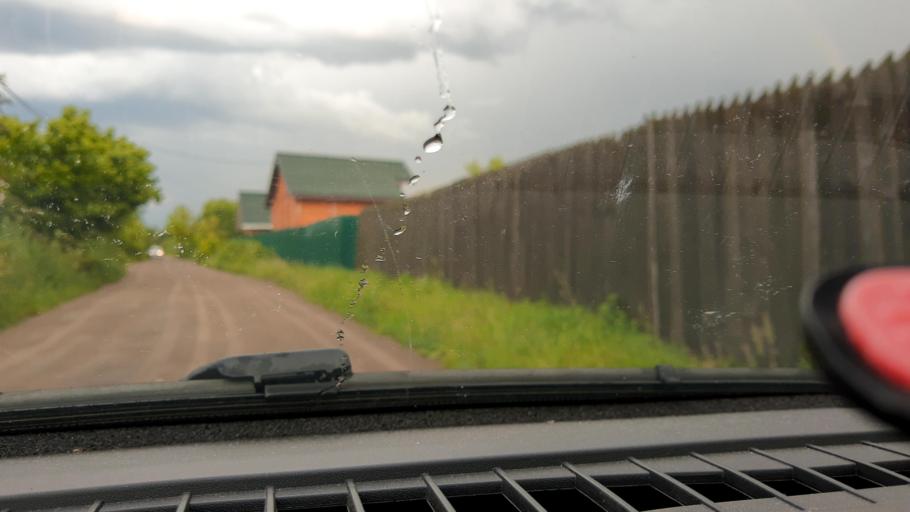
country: RU
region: Nizjnij Novgorod
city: Zavolzh'ye
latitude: 56.6592
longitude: 43.4251
